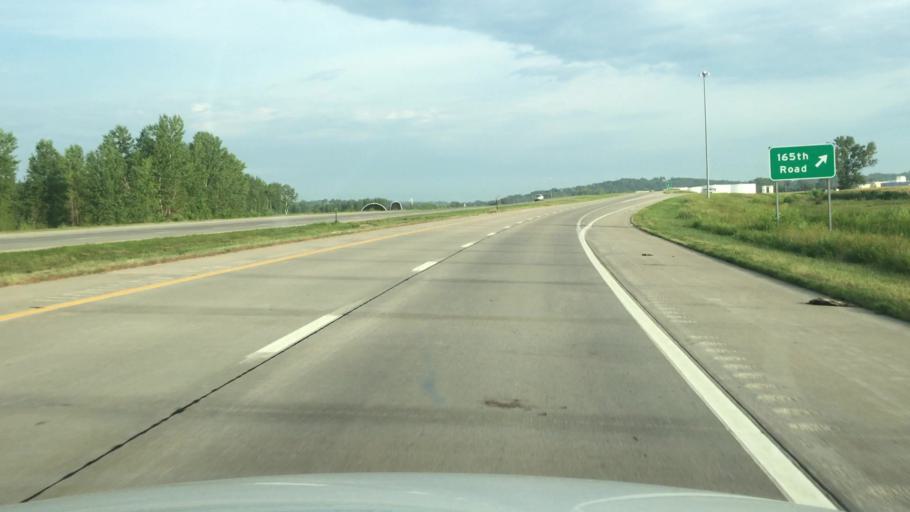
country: US
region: Kansas
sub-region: Doniphan County
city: Wathena
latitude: 39.7431
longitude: -94.9204
